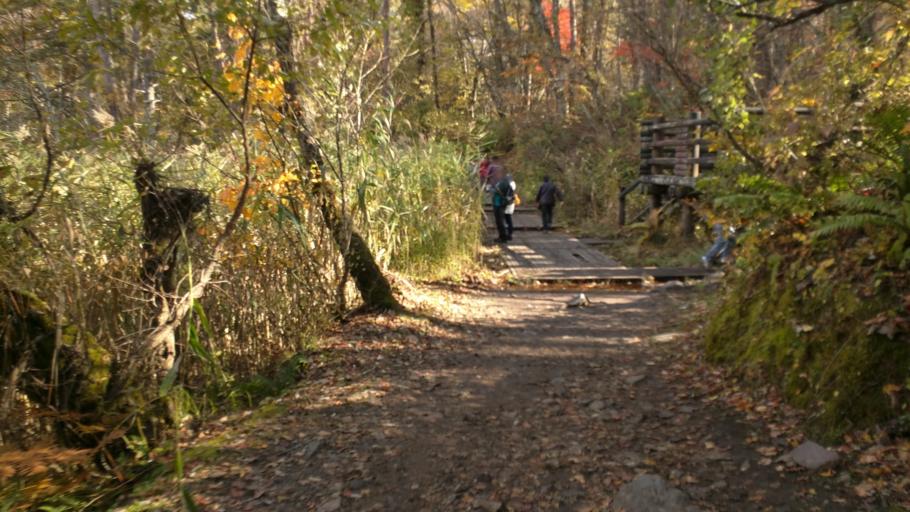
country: JP
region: Fukushima
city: Inawashiro
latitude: 37.6498
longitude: 140.0737
